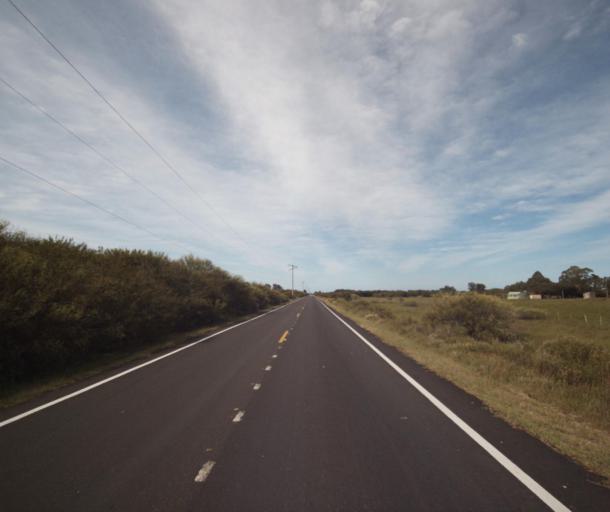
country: BR
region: Rio Grande do Sul
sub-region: Rio Grande
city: Rio Grande
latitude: -31.9167
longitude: -51.9428
